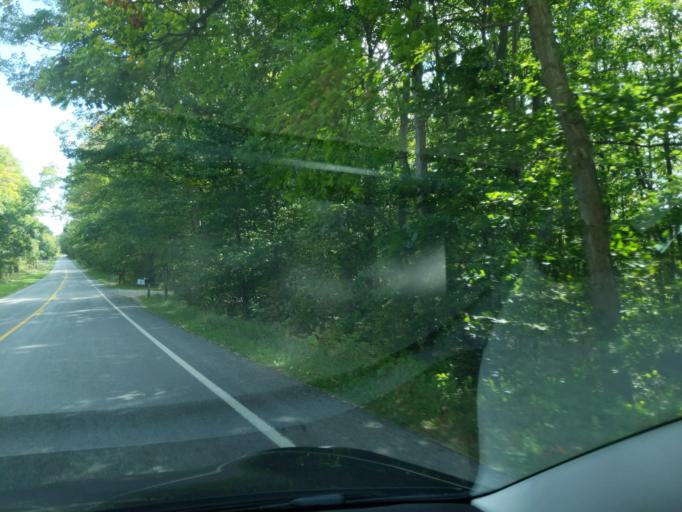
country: US
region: Michigan
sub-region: Antrim County
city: Bellaire
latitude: 44.9971
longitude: -85.2897
